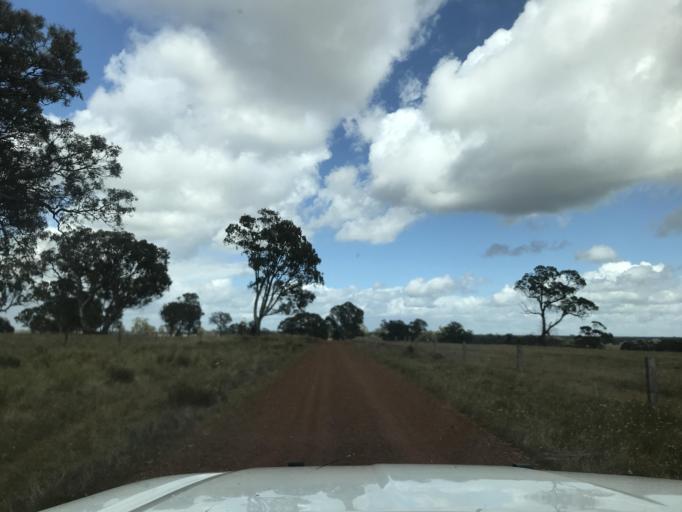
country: AU
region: South Australia
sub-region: Wattle Range
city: Penola
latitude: -37.1938
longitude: 141.4212
